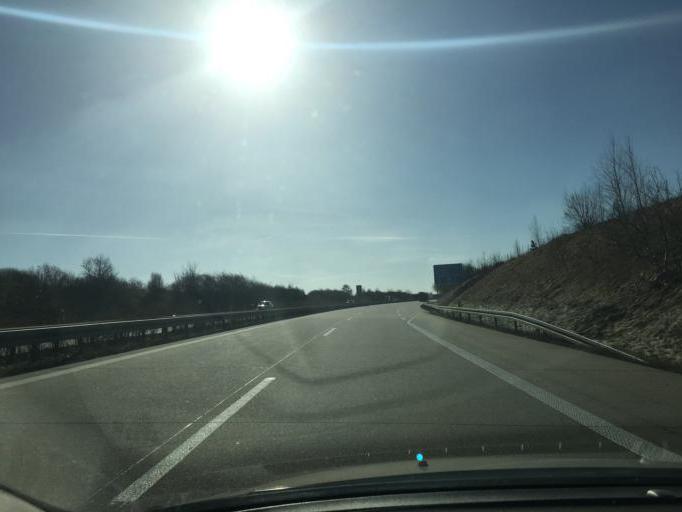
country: DE
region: Saxony
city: Muhlau
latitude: 50.8843
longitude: 12.7775
